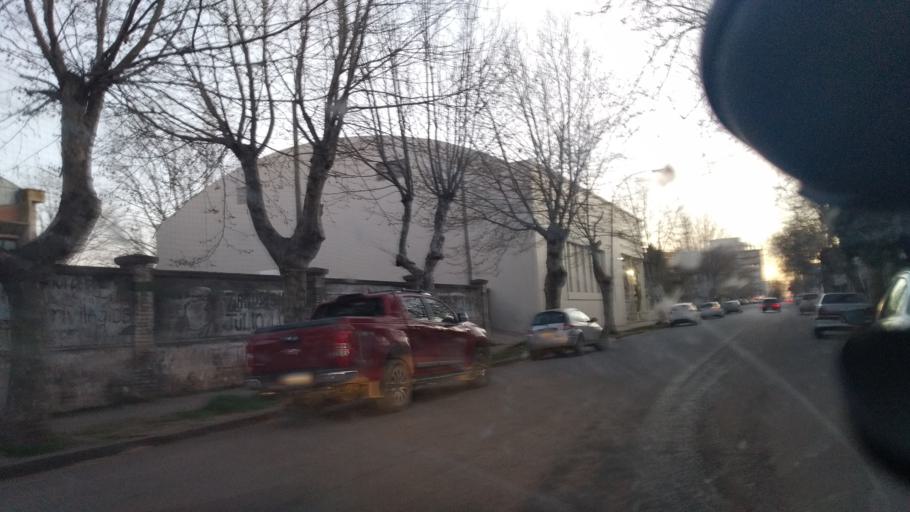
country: AR
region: Buenos Aires
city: Necochea
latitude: -38.5521
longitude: -58.7384
